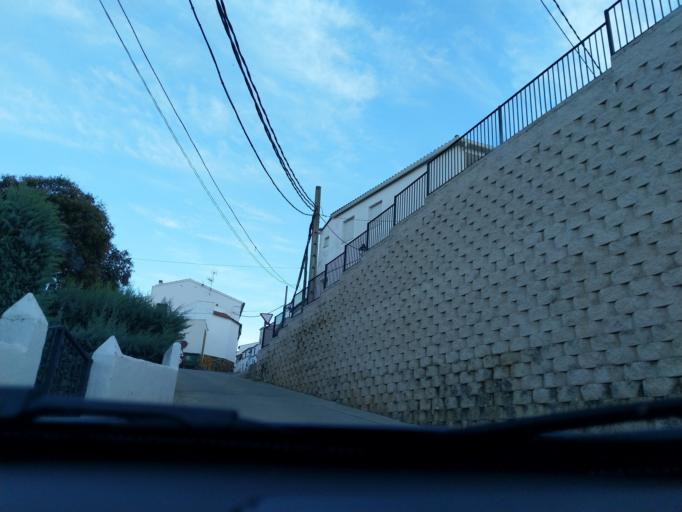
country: ES
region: Extremadura
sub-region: Provincia de Badajoz
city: Reina
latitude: 38.1876
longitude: -5.9498
